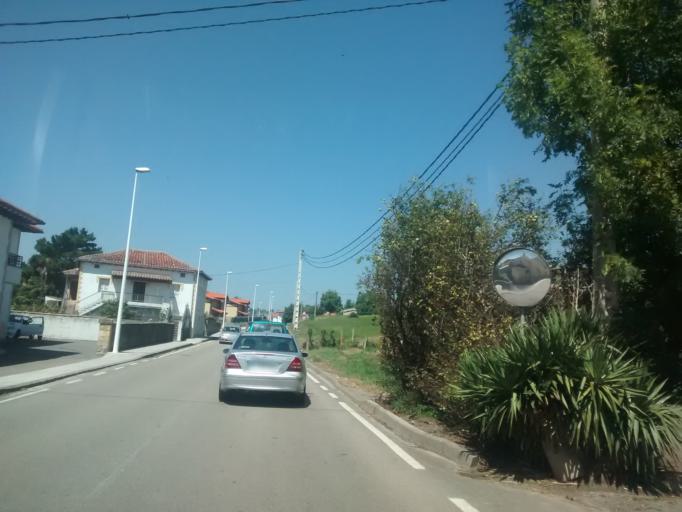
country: ES
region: Cantabria
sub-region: Provincia de Cantabria
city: San Miguel de Meruelo
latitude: 43.4575
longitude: -3.5796
